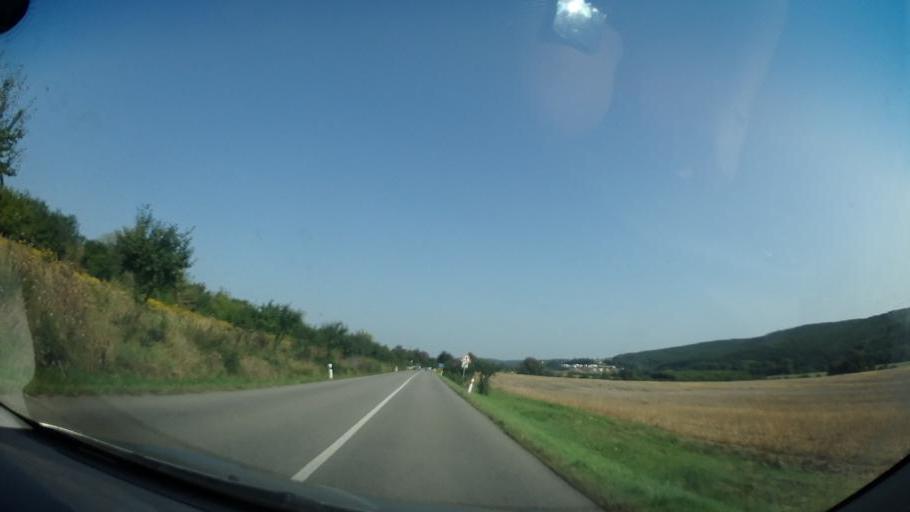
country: CZ
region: South Moravian
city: Kurim
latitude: 49.2523
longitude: 16.5245
